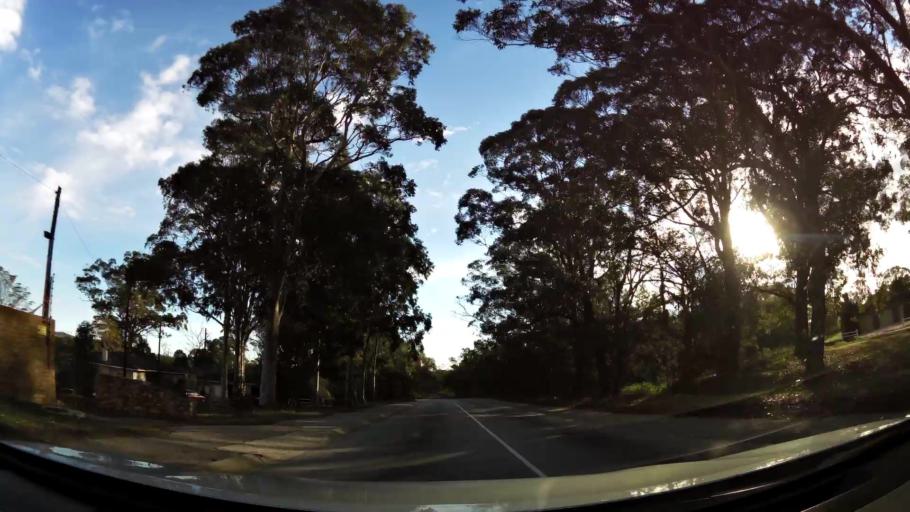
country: ZA
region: Eastern Cape
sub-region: Nelson Mandela Bay Metropolitan Municipality
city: Port Elizabeth
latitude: -33.9560
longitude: 25.5175
